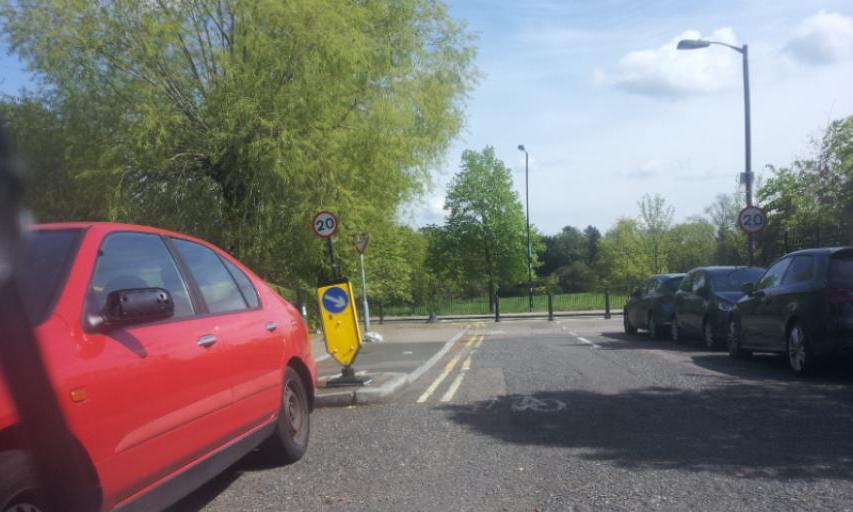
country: GB
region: England
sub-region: Greater London
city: Camberwell
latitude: 51.4566
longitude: -0.0650
